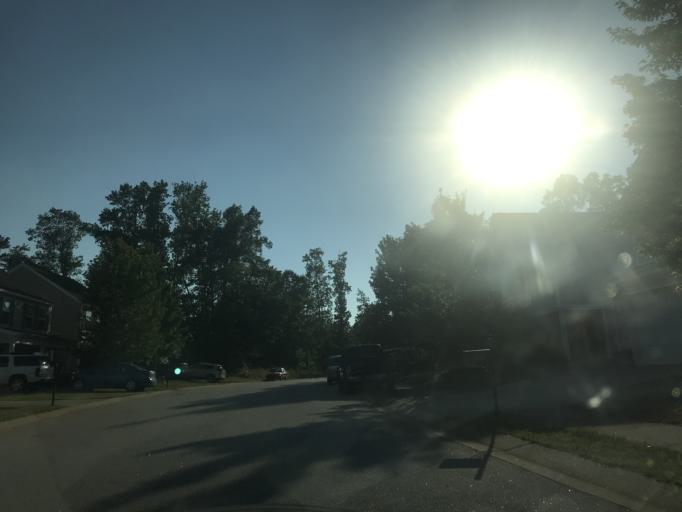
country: US
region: North Carolina
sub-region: Wake County
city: Garner
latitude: 35.7327
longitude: -78.6208
